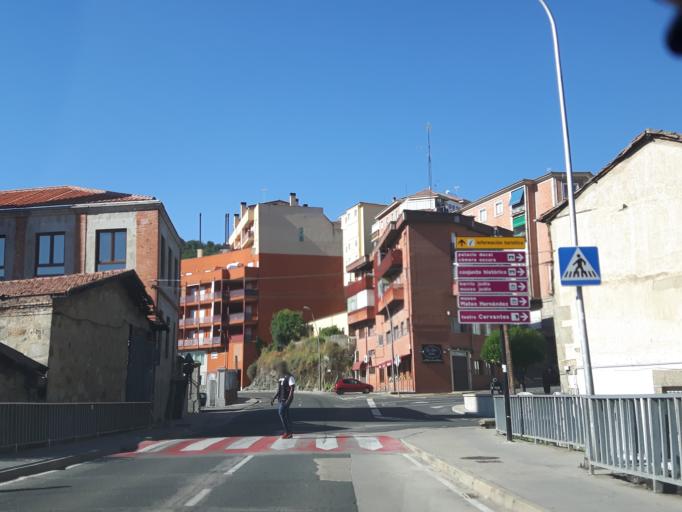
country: ES
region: Castille and Leon
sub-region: Provincia de Salamanca
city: Bejar
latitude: 40.3867
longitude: -5.7598
